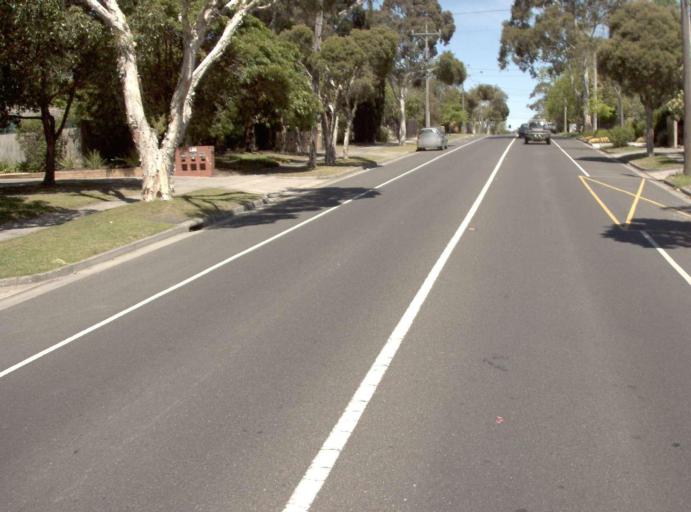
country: AU
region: Victoria
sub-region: Whitehorse
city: Blackburn North
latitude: -37.8083
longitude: 145.1582
